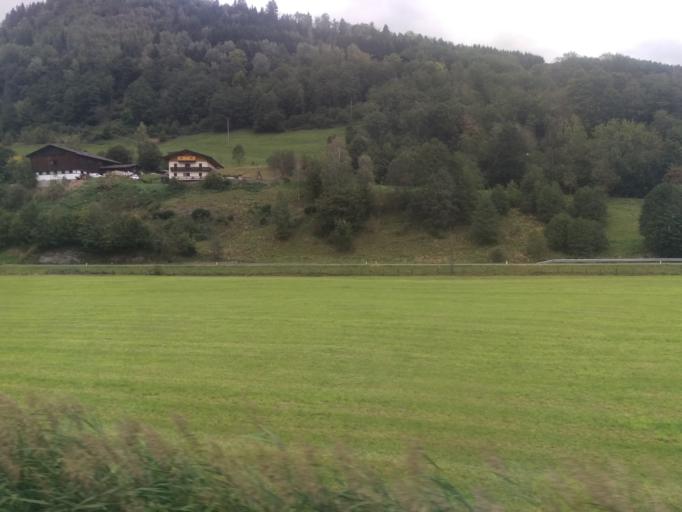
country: AT
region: Salzburg
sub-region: Politischer Bezirk Zell am See
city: Niedernsill
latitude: 47.2846
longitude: 12.6756
